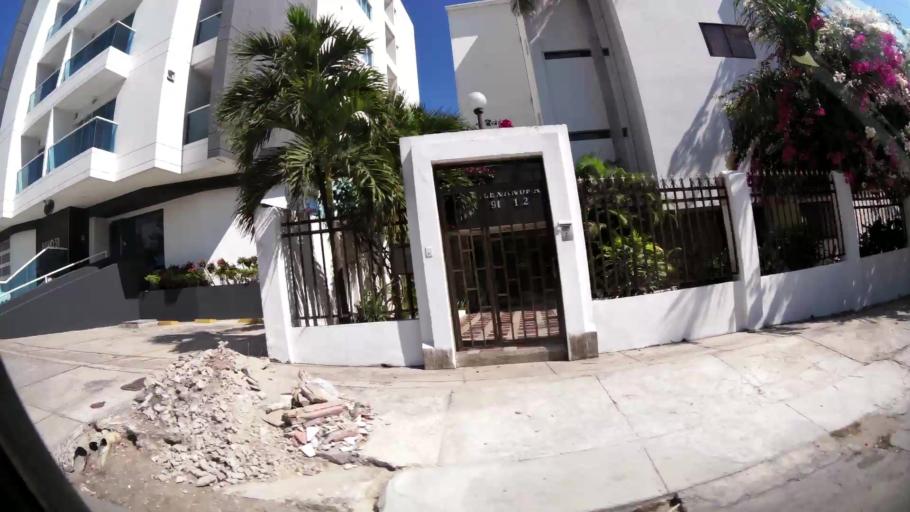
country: CO
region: Atlantico
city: Barranquilla
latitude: 11.0126
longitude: -74.8226
